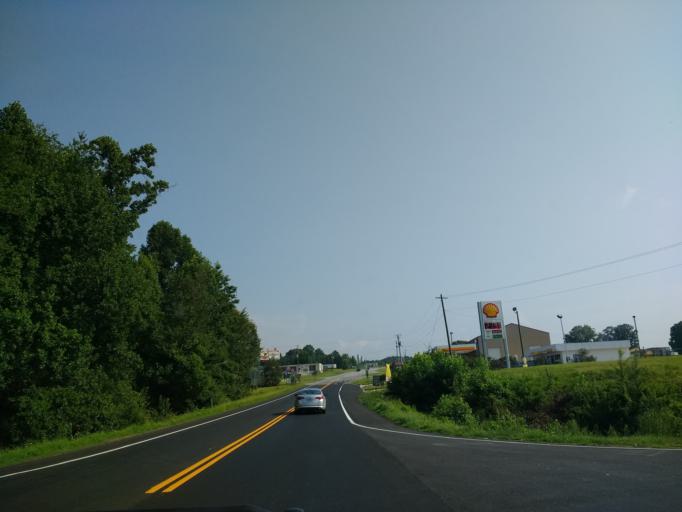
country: US
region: Georgia
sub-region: White County
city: Cleveland
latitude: 34.5032
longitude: -83.7566
